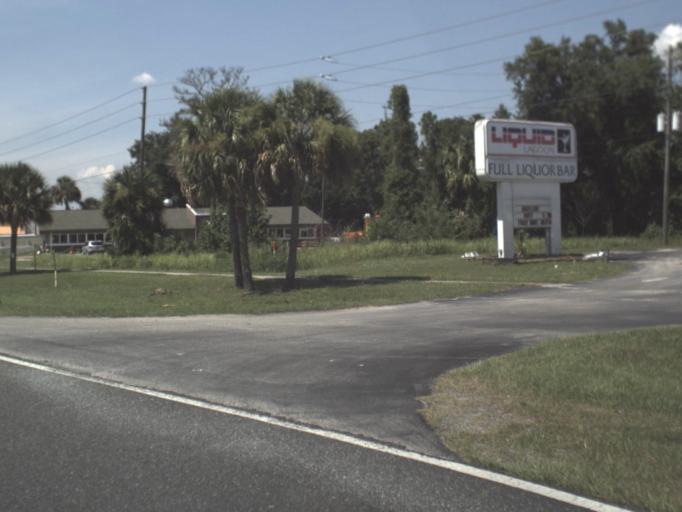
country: US
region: Florida
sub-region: Citrus County
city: Crystal River
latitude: 28.8796
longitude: -82.5814
